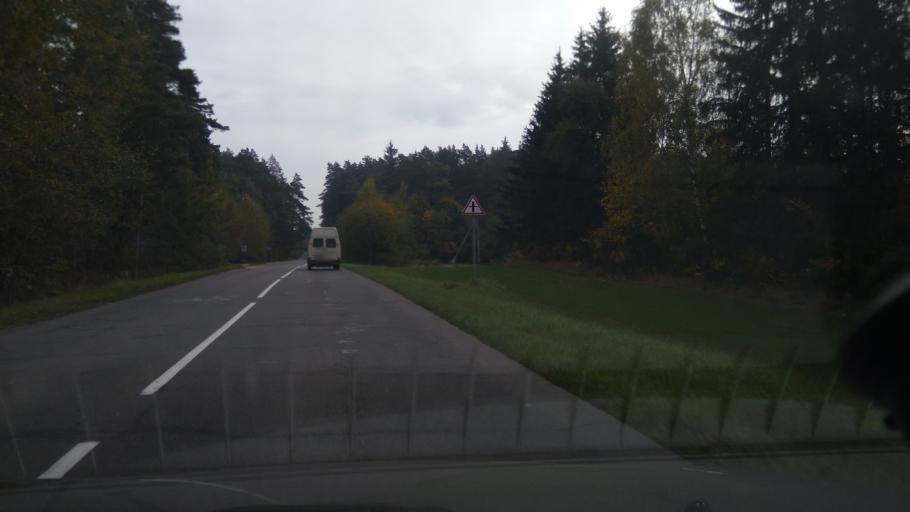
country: BY
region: Minsk
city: Rudzyensk
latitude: 53.6142
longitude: 27.7687
